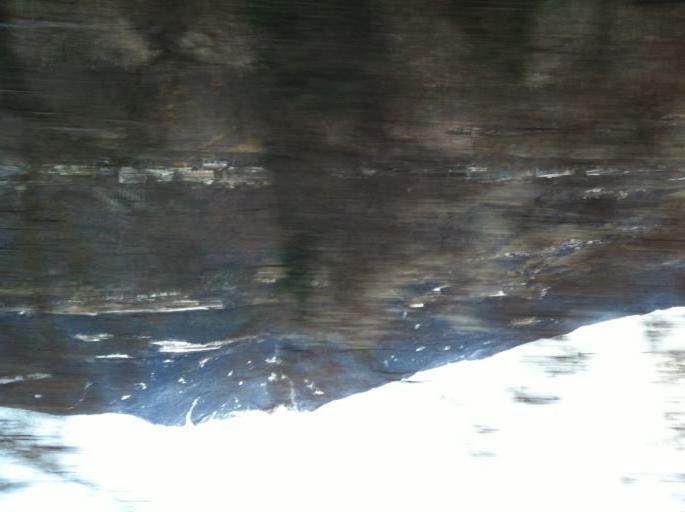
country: IT
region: Trentino-Alto Adige
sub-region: Bolzano
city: Bressanone
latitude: 46.6980
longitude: 11.6593
